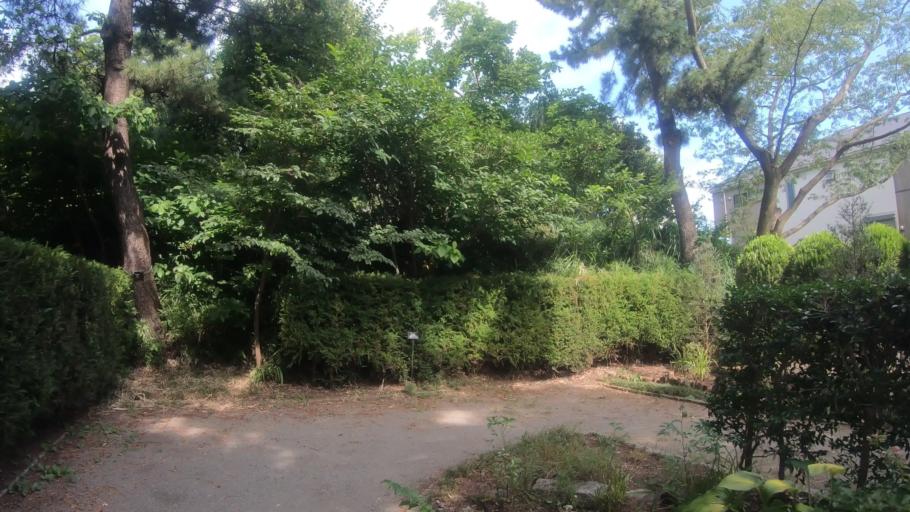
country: JP
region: Kanagawa
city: Yokohama
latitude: 35.4324
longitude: 139.5781
